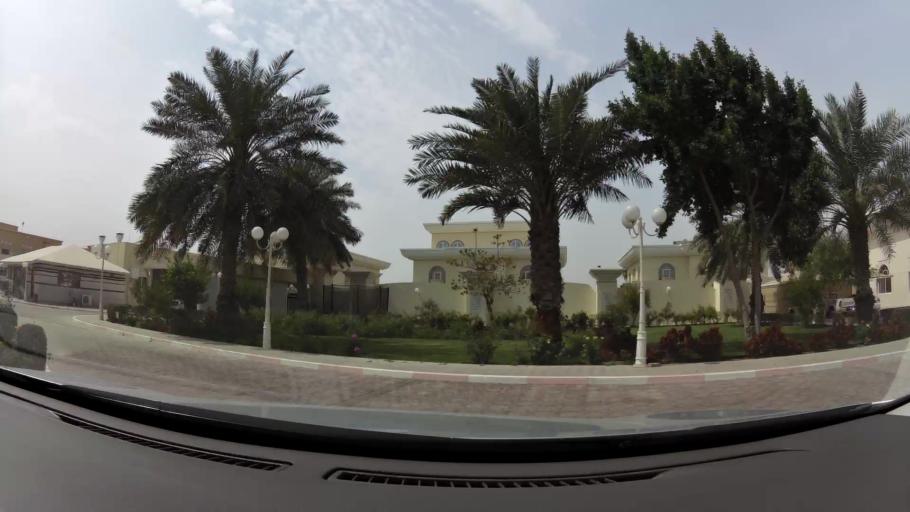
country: QA
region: Baladiyat ad Dawhah
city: Doha
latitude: 25.2658
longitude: 51.4914
